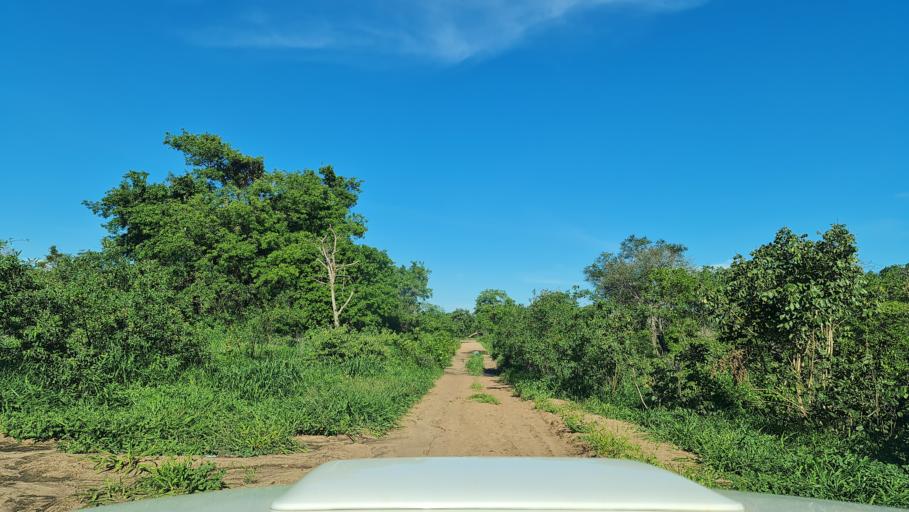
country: MZ
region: Nampula
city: Ilha de Mocambique
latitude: -15.2692
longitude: 40.1868
